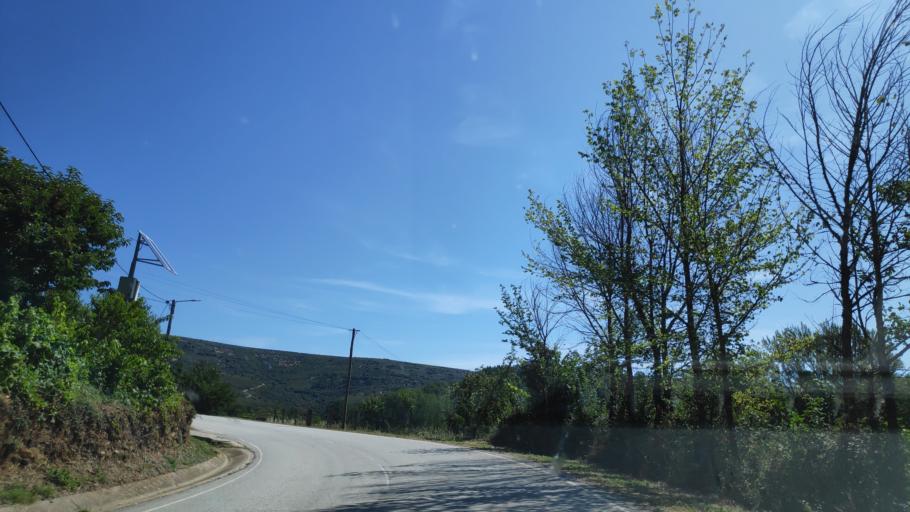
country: PT
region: Braganca
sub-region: Braganca Municipality
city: Braganca
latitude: 41.9031
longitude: -6.7339
